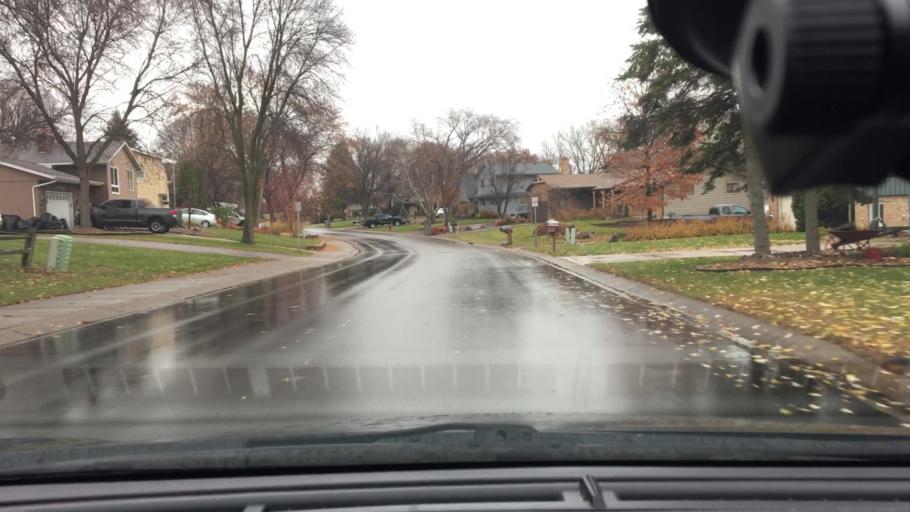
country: US
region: Minnesota
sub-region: Hennepin County
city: Corcoran
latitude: 45.1116
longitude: -93.5091
